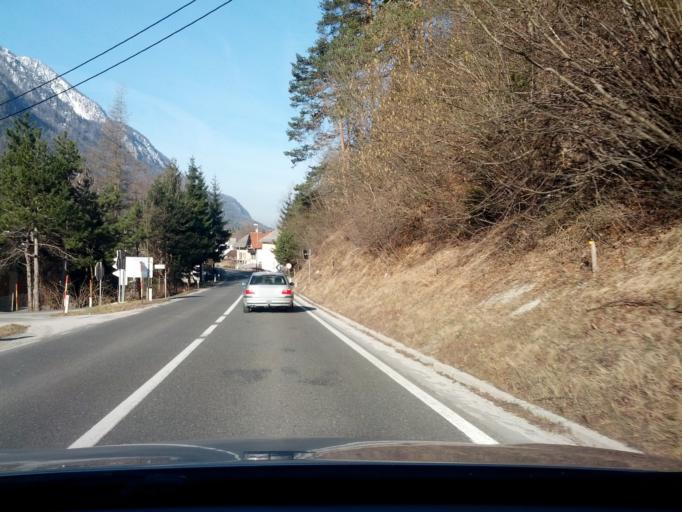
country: SI
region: Kranjska Gora
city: Mojstrana
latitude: 46.4671
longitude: 13.9336
